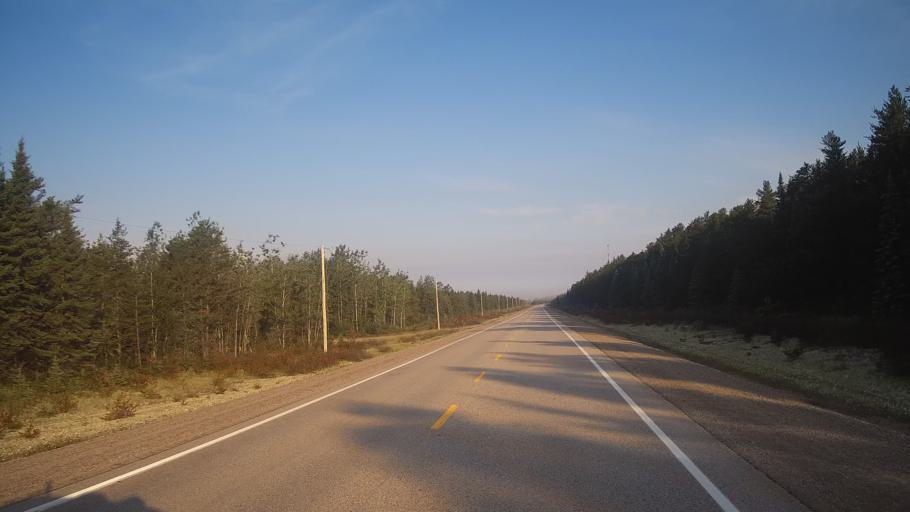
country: CA
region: Ontario
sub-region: Rainy River District
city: Atikokan
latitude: 49.3272
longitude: -91.4220
